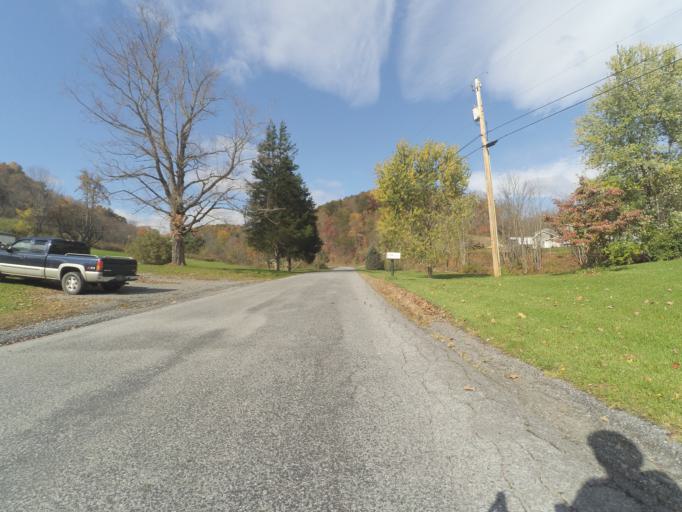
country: US
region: Pennsylvania
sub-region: Centre County
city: Park Forest Village
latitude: 40.8598
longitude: -77.9531
